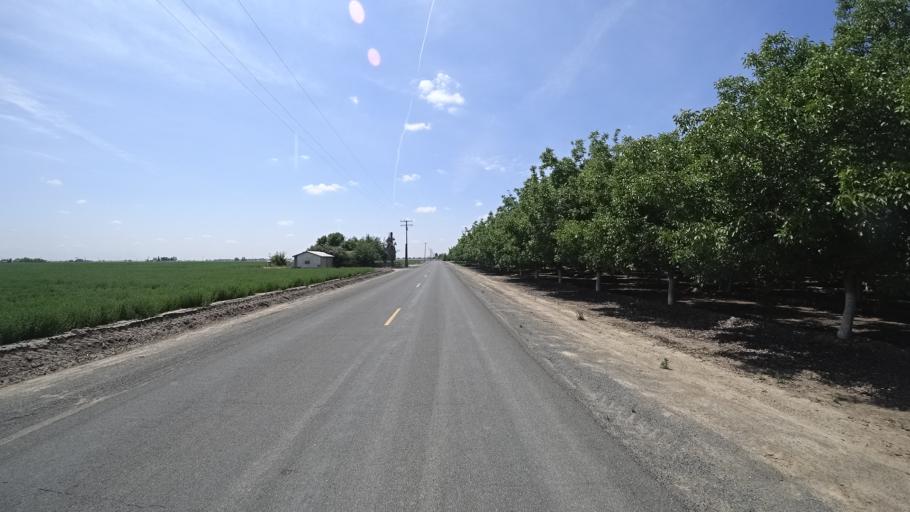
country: US
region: California
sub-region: Tulare County
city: Goshen
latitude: 36.3193
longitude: -119.4753
